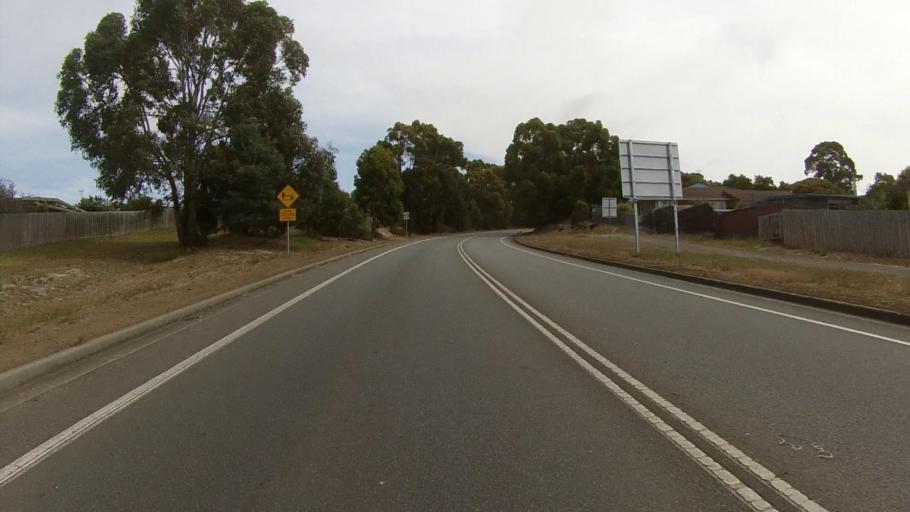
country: AU
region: Tasmania
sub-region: Kingborough
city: Blackmans Bay
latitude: -42.9992
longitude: 147.3172
